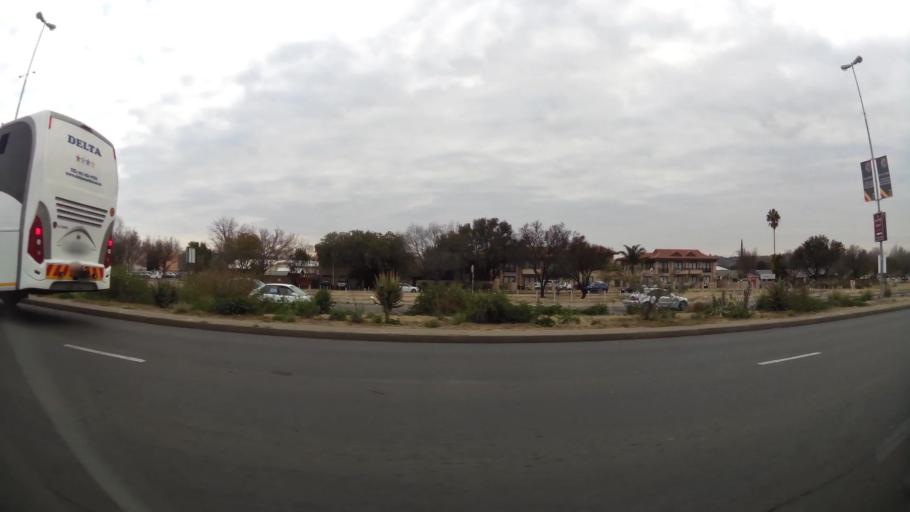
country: ZA
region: Orange Free State
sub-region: Mangaung Metropolitan Municipality
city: Bloemfontein
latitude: -29.1073
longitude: 26.1946
